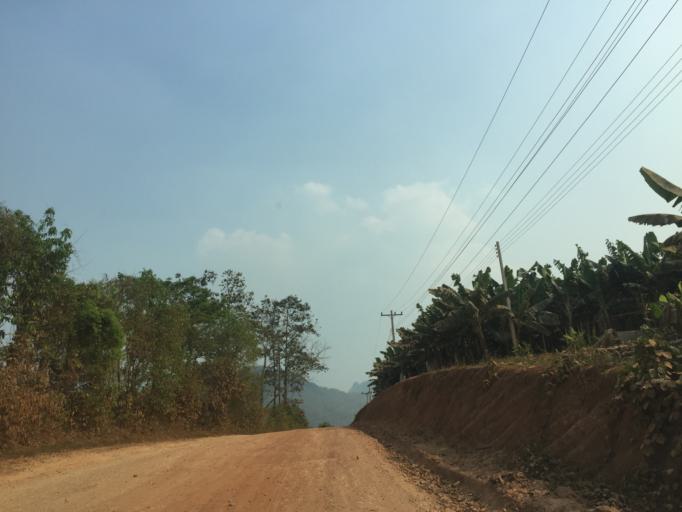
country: LA
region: Xiagnabouli
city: Sainyabuli
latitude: 19.2124
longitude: 101.6936
